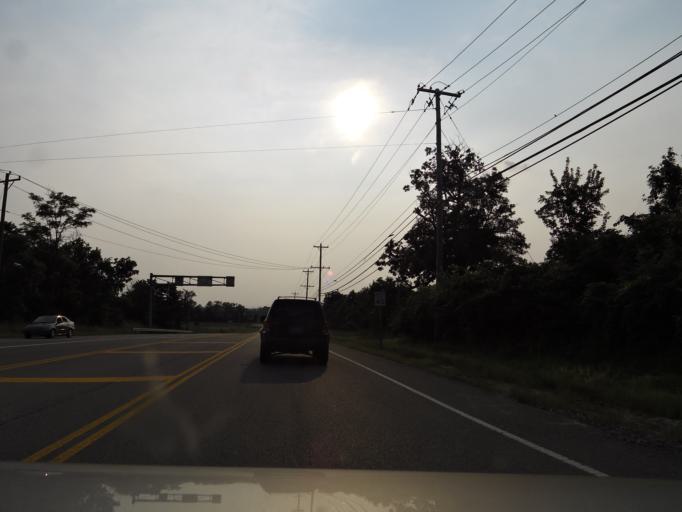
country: US
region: Ohio
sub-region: Butler County
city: Hamilton
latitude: 39.3789
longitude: -84.5075
